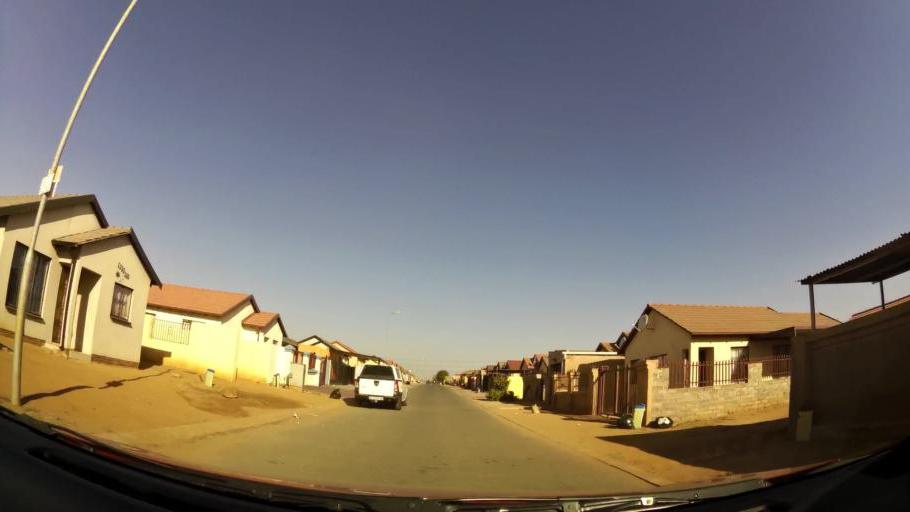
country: ZA
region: Gauteng
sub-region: City of Tshwane Metropolitan Municipality
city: Mabopane
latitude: -25.5739
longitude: 28.0886
